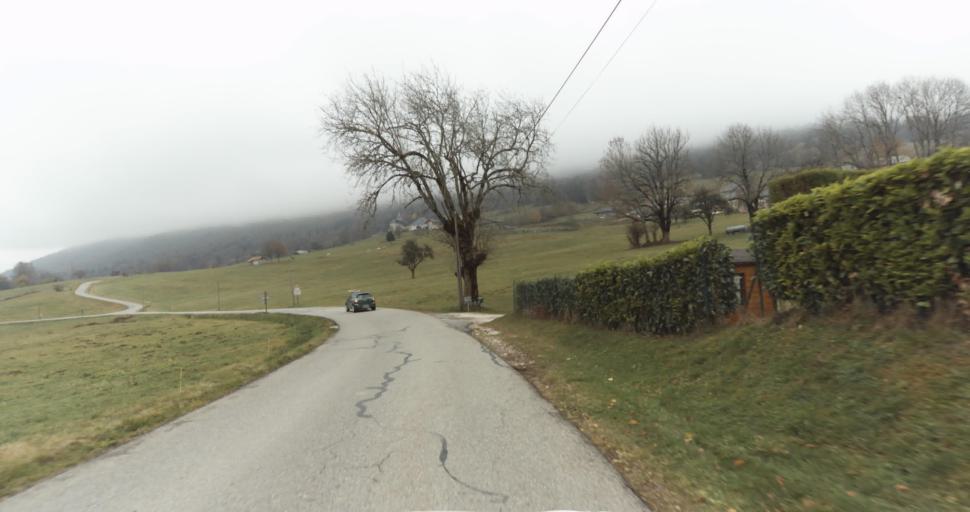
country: FR
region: Rhone-Alpes
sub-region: Departement de la Haute-Savoie
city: Saint-Jorioz
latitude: 45.7701
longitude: 6.1288
